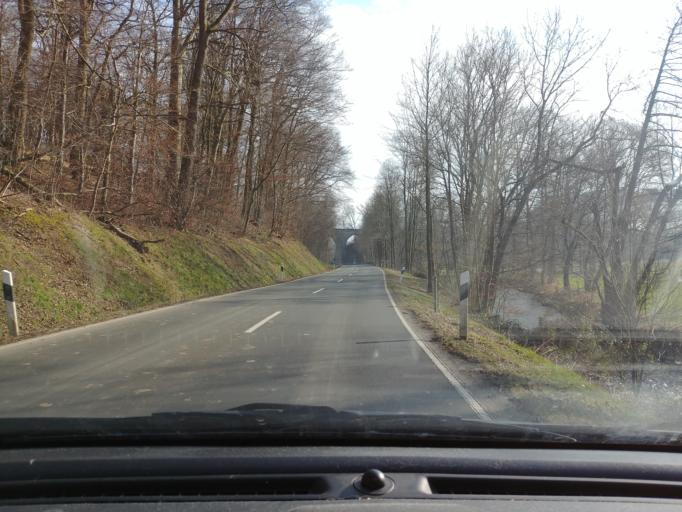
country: DE
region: Lower Saxony
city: Uslar
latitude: 51.6455
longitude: 9.6377
